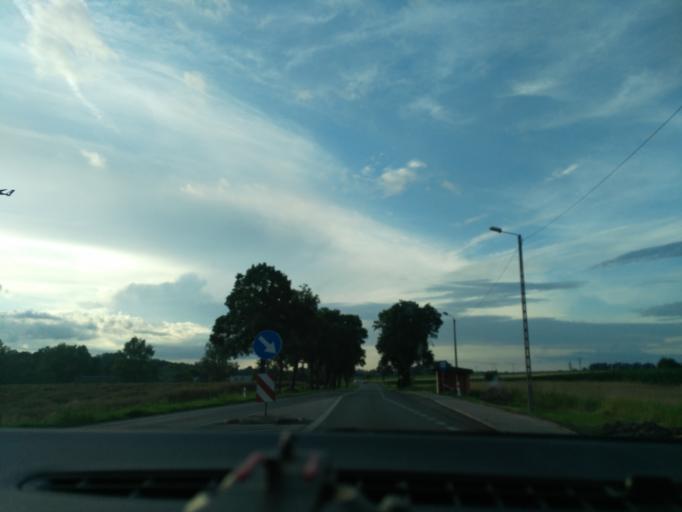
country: PL
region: Lublin Voivodeship
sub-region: Powiat lubelski
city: Niedrzwica Duza
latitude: 51.0783
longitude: 22.3741
